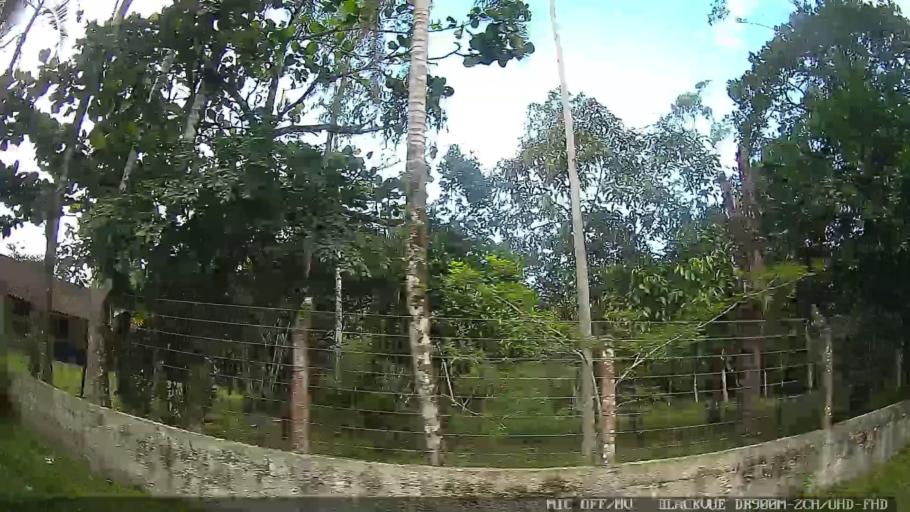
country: BR
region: Sao Paulo
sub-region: Itanhaem
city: Itanhaem
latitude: -24.1747
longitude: -46.9323
